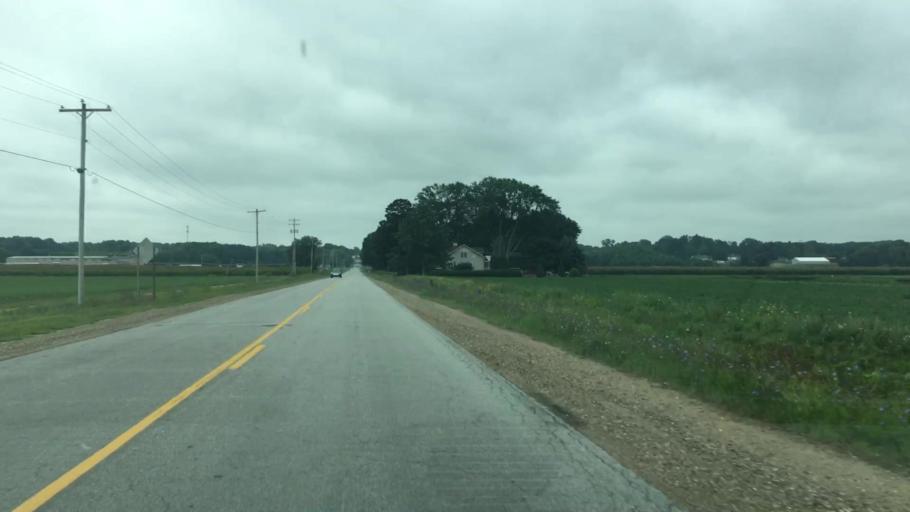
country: US
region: Michigan
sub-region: Ottawa County
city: Hudsonville
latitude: 42.8694
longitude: -85.8365
